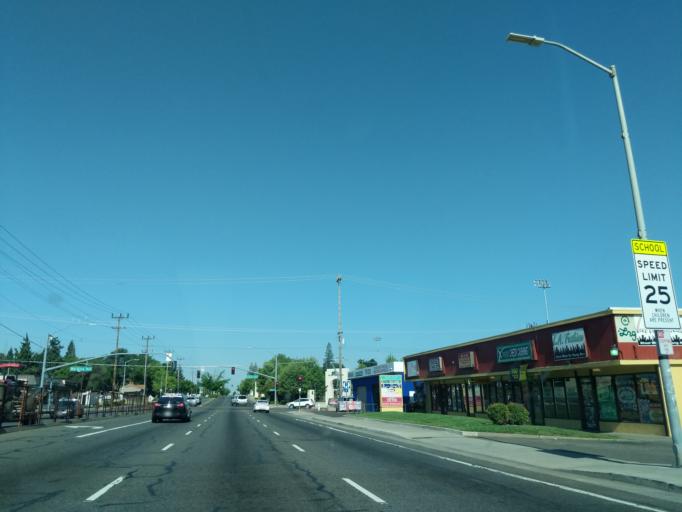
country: US
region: California
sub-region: Sacramento County
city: Citrus Heights
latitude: 38.6783
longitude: -121.2836
